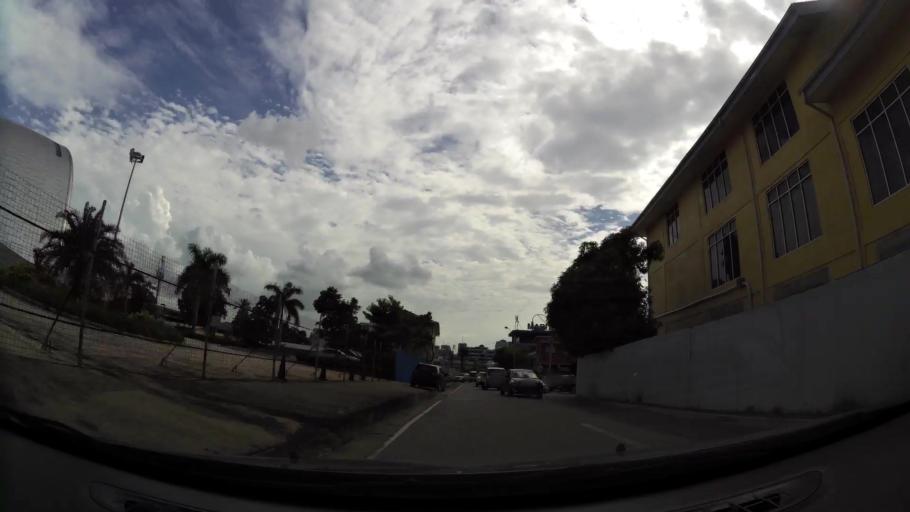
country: TT
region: City of Port of Spain
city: Port-of-Spain
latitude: 10.6634
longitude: -61.5126
